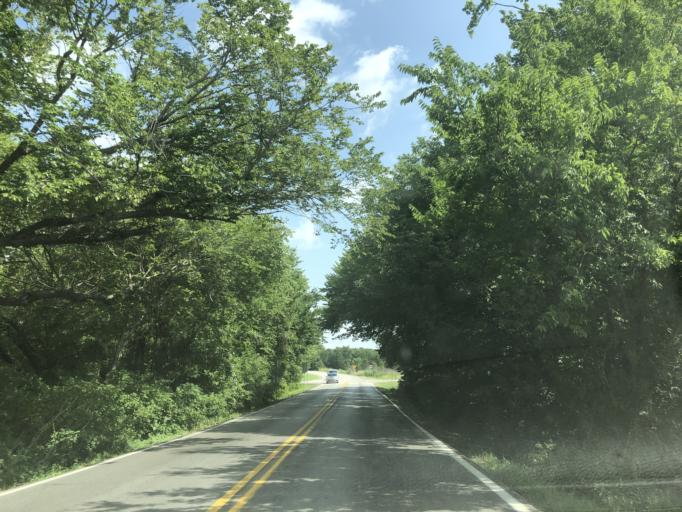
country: US
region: Texas
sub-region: Dallas County
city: Sunnyvale
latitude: 32.8327
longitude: -96.5599
